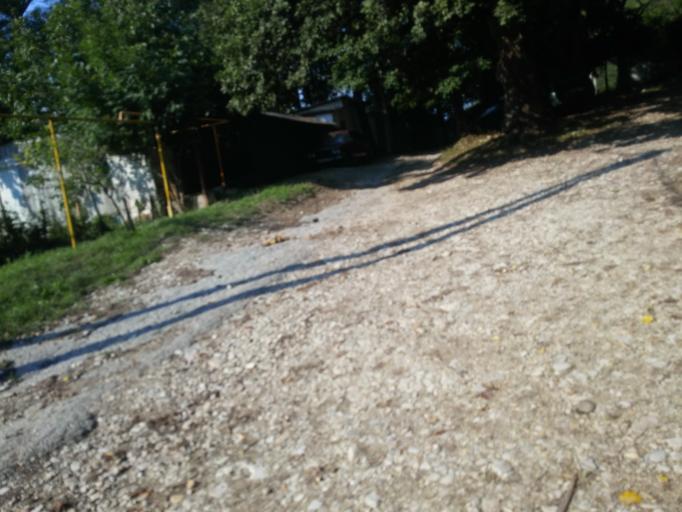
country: RU
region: Krasnodarskiy
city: Divnomorskoye
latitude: 44.4673
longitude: 38.1633
